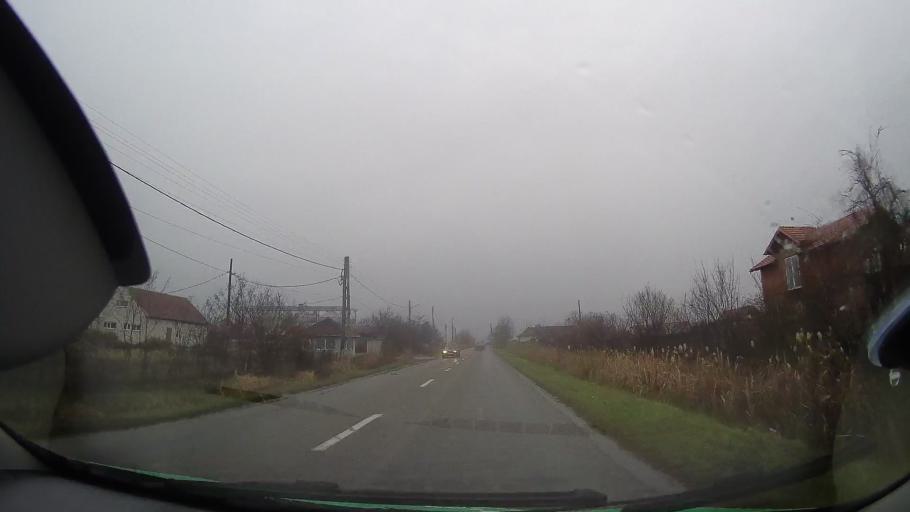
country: RO
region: Bihor
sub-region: Comuna Tulca
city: Tulca
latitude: 46.7939
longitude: 21.7441
